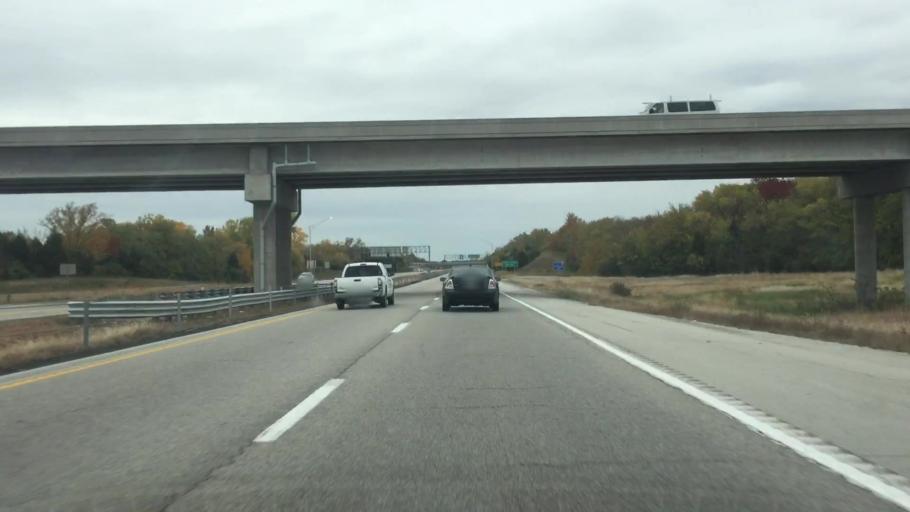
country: US
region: Missouri
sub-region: Jackson County
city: Lees Summit
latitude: 38.9358
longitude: -94.4067
